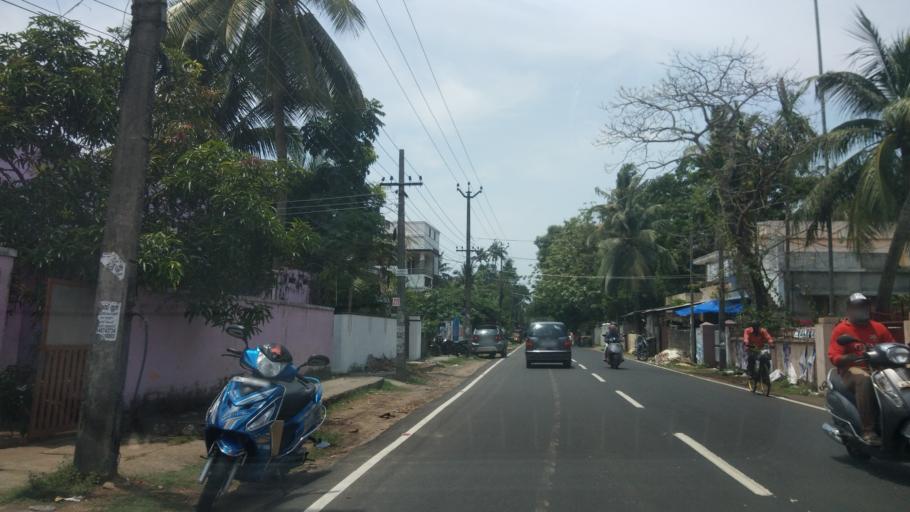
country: IN
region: Kerala
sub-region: Ernakulam
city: Cochin
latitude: 9.9314
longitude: 76.2472
